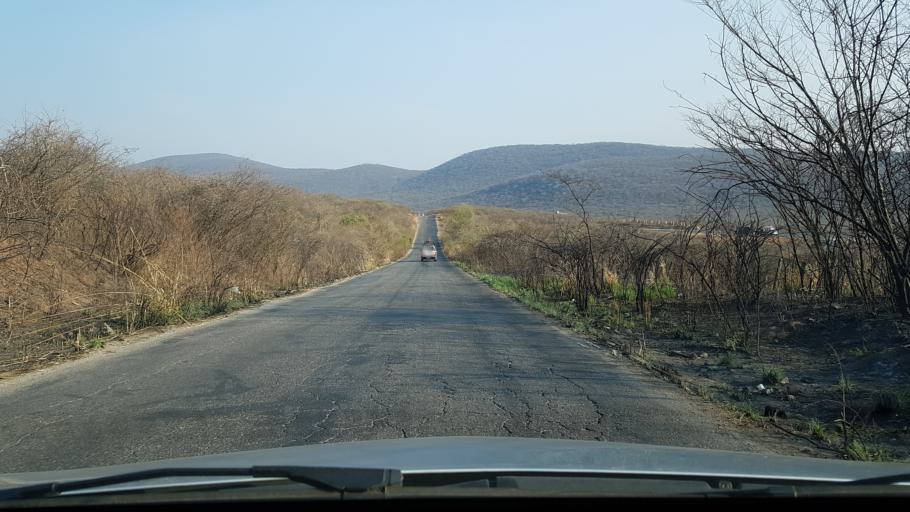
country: MX
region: Morelos
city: Tlaltizapan
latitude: 18.6672
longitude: -99.0528
